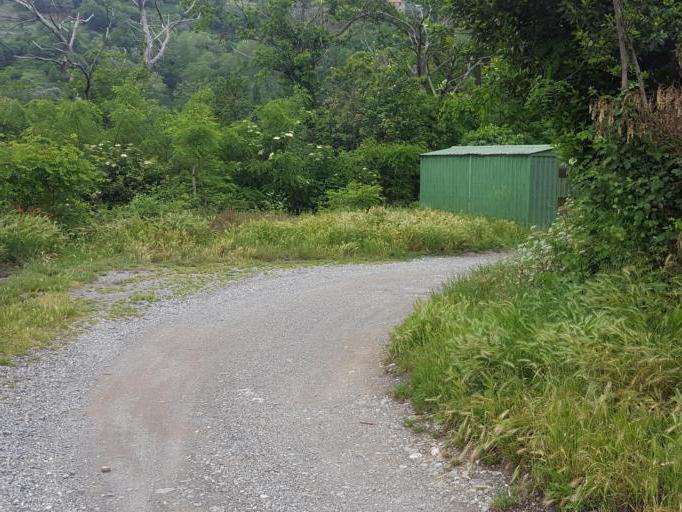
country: IT
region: Liguria
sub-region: Provincia di Genova
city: Manesseno
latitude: 44.4590
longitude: 8.9139
